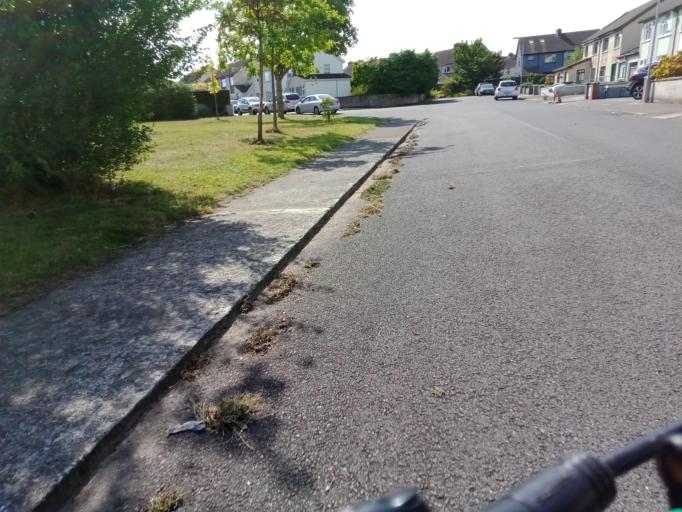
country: IE
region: Munster
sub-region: Waterford
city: Dungarvan
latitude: 52.0939
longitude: -7.6038
